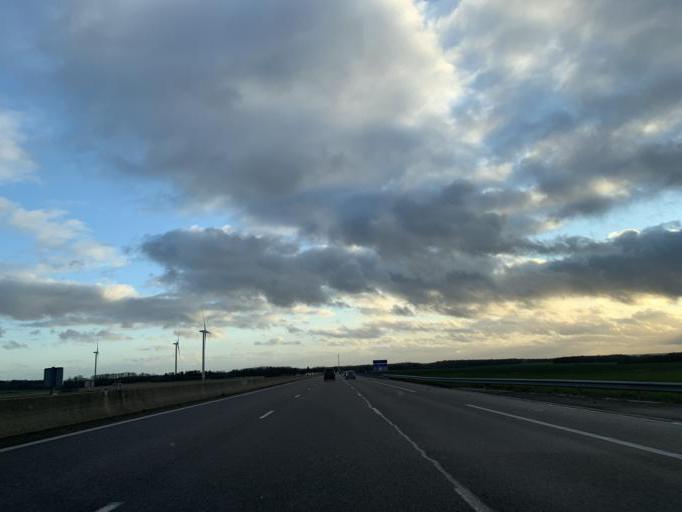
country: FR
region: Bourgogne
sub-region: Departement de la Cote-d'Or
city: Selongey
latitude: 47.7036
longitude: 5.1870
